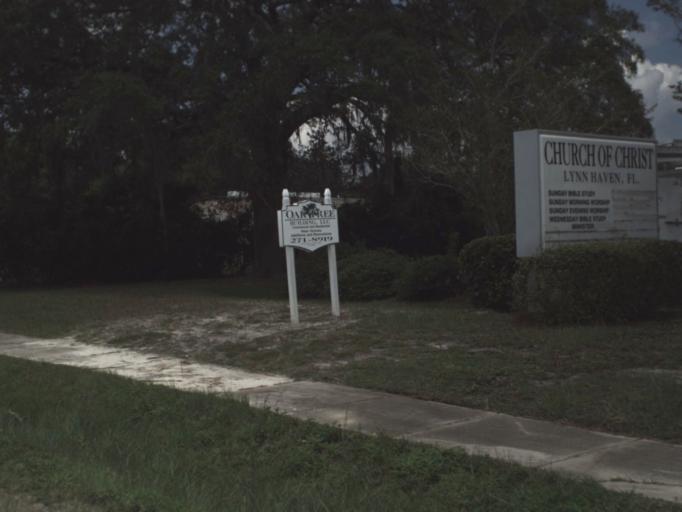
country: US
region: Florida
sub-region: Bay County
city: Lynn Haven
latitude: 30.2375
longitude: -85.6433
